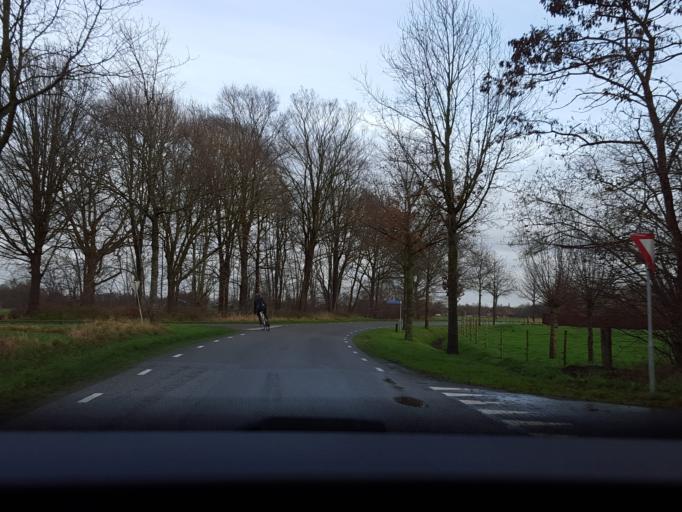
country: NL
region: Gelderland
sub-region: Oude IJsselstreek
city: Varsseveld
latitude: 52.0172
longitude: 6.4876
